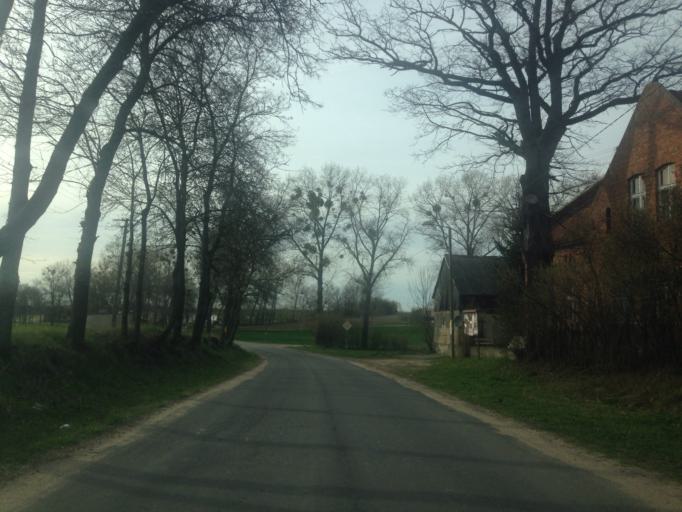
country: PL
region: Kujawsko-Pomorskie
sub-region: Powiat brodnicki
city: Jablonowo Pomorskie
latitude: 53.3987
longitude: 19.2255
